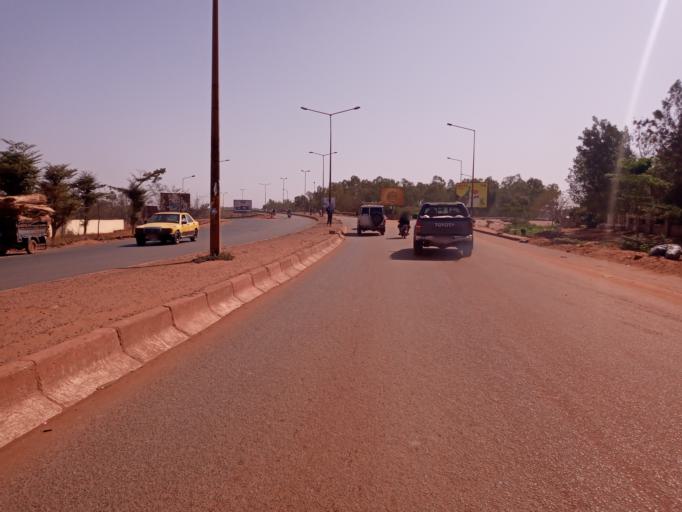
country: ML
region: Bamako
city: Bamako
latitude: 12.6076
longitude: -7.9991
